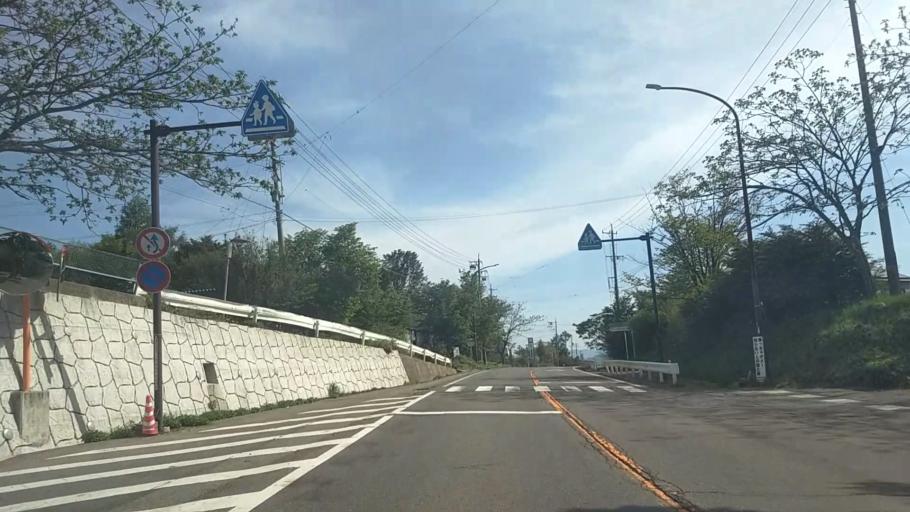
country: JP
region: Nagano
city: Saku
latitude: 35.9768
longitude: 138.4811
